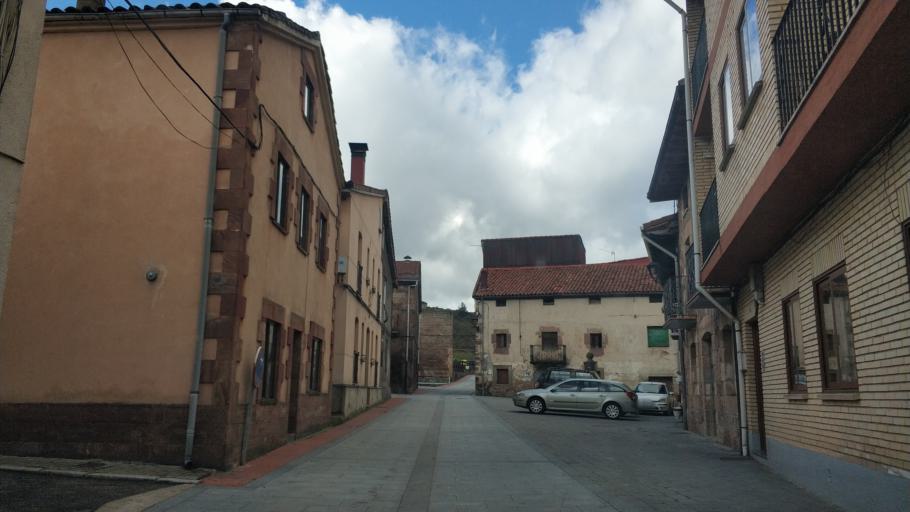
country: ES
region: Castille and Leon
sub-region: Provincia de Burgos
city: Neila
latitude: 42.0606
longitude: -2.9979
